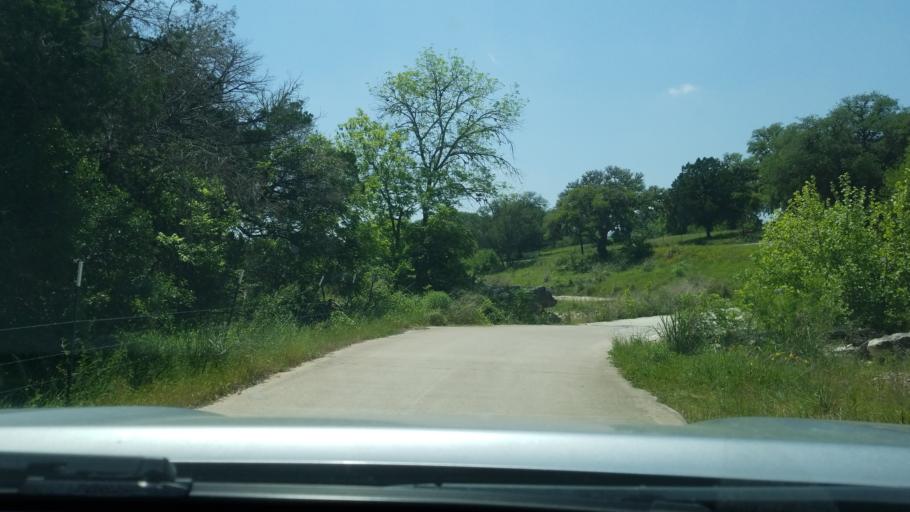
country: US
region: Texas
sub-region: Blanco County
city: Blanco
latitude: 30.0014
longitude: -98.4140
